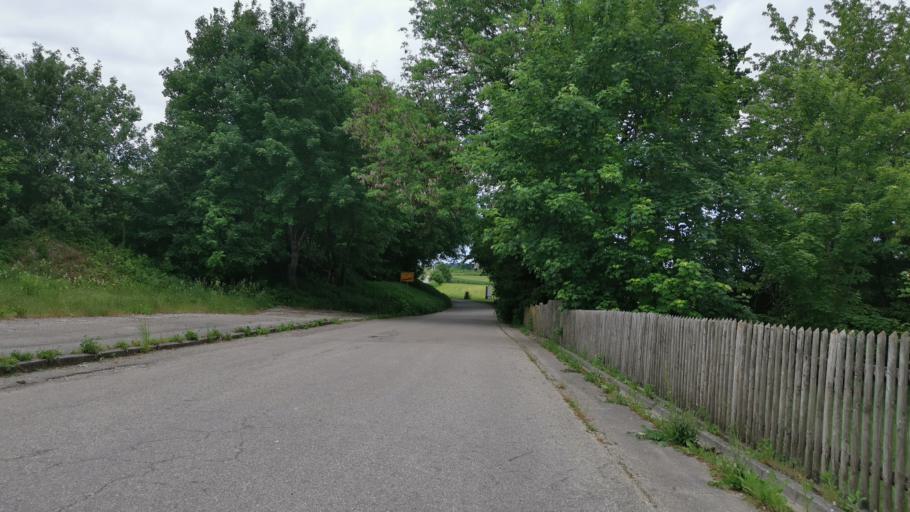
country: DE
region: Bavaria
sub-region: Upper Bavaria
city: Althegnenberg
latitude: 48.2373
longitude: 11.0615
